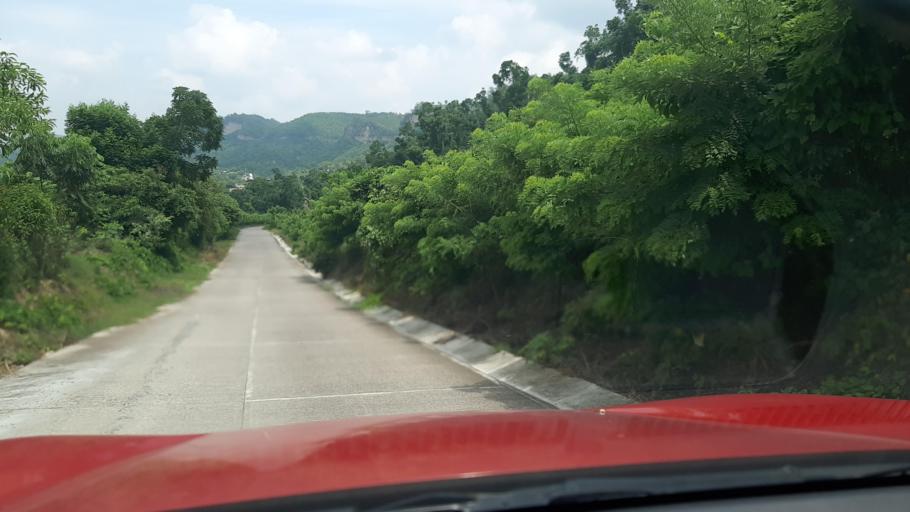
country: MX
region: Veracruz
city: Gutierrez Zamora
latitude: 20.4601
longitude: -97.1832
